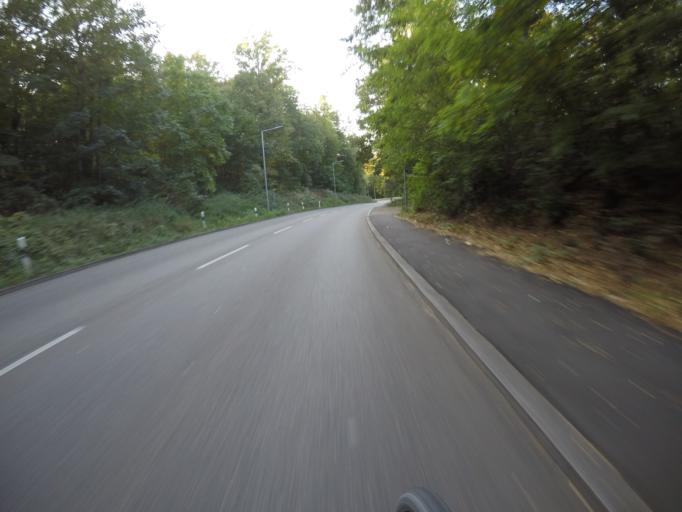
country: DE
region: Baden-Wuerttemberg
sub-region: Regierungsbezirk Stuttgart
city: Ostfildern
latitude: 48.7547
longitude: 9.2425
